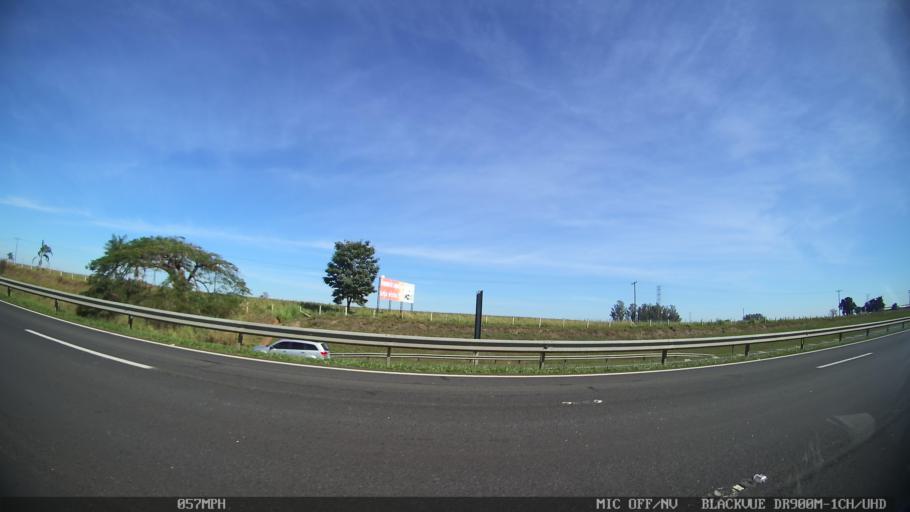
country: BR
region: Sao Paulo
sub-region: Pirassununga
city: Pirassununga
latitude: -22.0838
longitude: -47.4206
